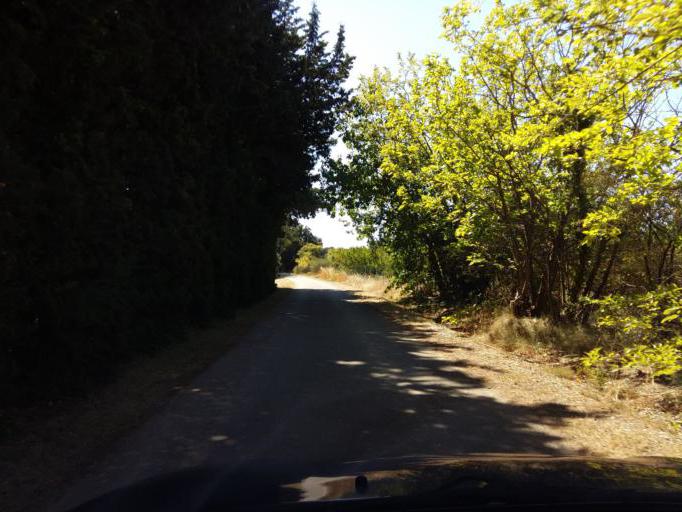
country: FR
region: Provence-Alpes-Cote d'Azur
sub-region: Departement du Vaucluse
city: Loriol-du-Comtat
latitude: 44.0892
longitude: 5.0060
